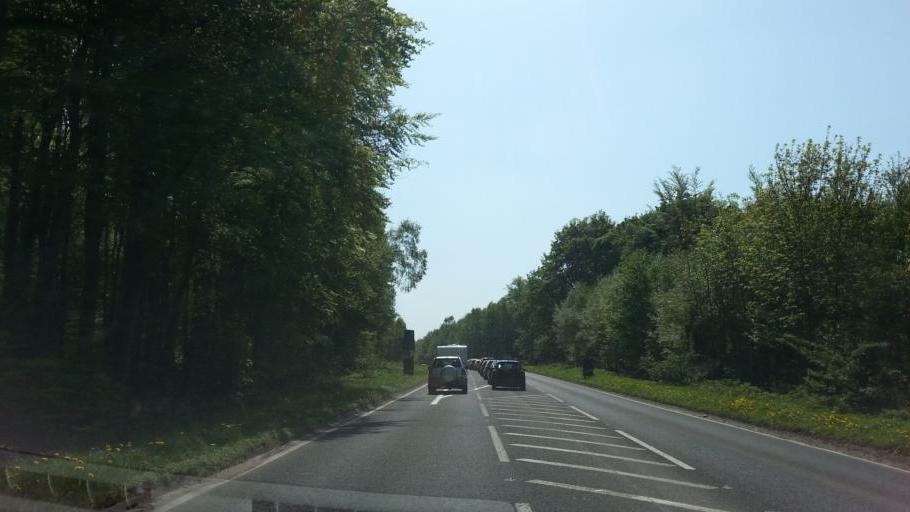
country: GB
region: England
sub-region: Nottinghamshire
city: Babworth
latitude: 53.2907
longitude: -1.0333
